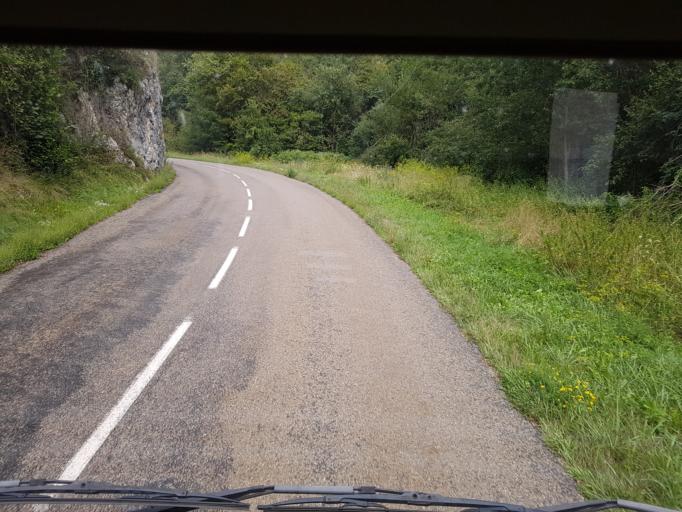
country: FR
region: Rhone-Alpes
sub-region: Departement de l'Ain
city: Saint-Martin-du-Frene
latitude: 46.1109
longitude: 5.4862
